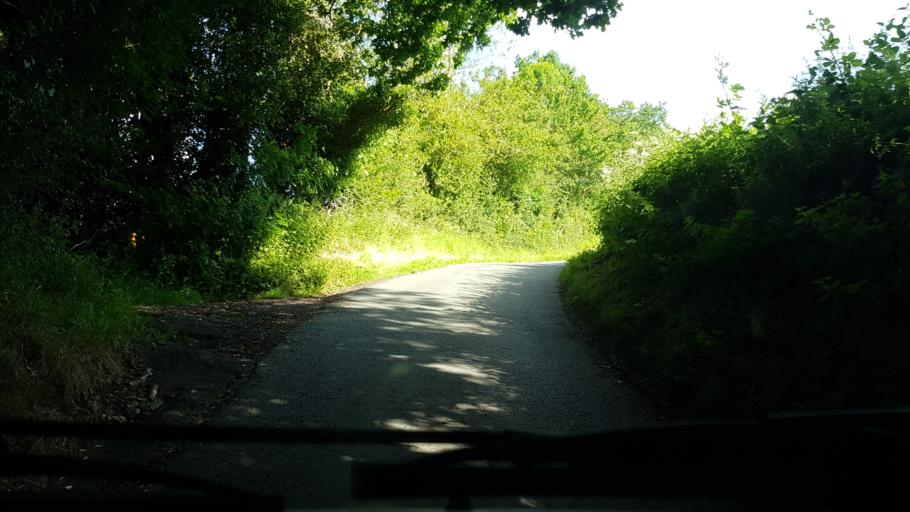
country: GB
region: England
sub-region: Worcestershire
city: Bewdley
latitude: 52.3463
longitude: -2.3306
